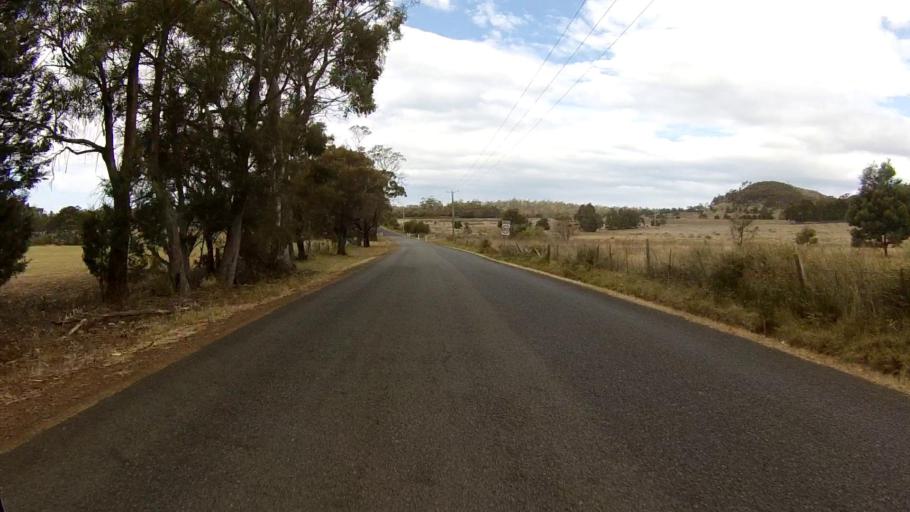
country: AU
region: Tasmania
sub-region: Sorell
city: Sorell
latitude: -42.5713
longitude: 147.8854
